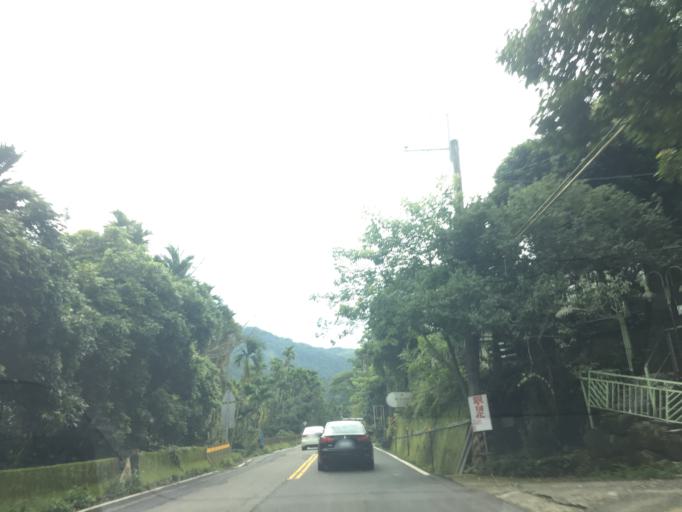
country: TW
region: Taiwan
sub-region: Chiayi
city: Jiayi Shi
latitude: 23.5619
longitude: 120.5747
